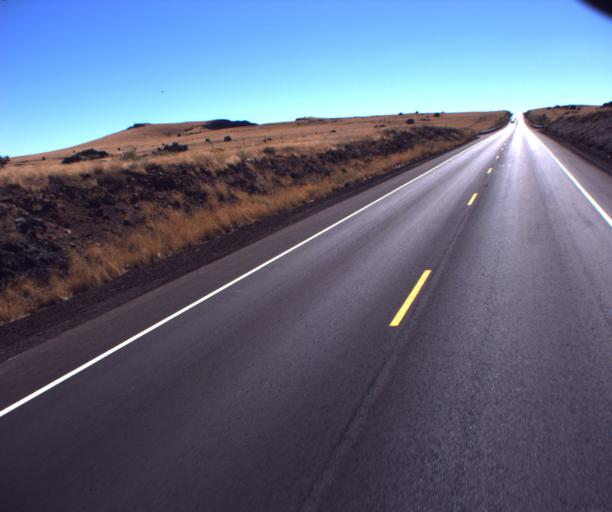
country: US
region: Arizona
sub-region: Apache County
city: Springerville
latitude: 34.2512
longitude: -109.3515
